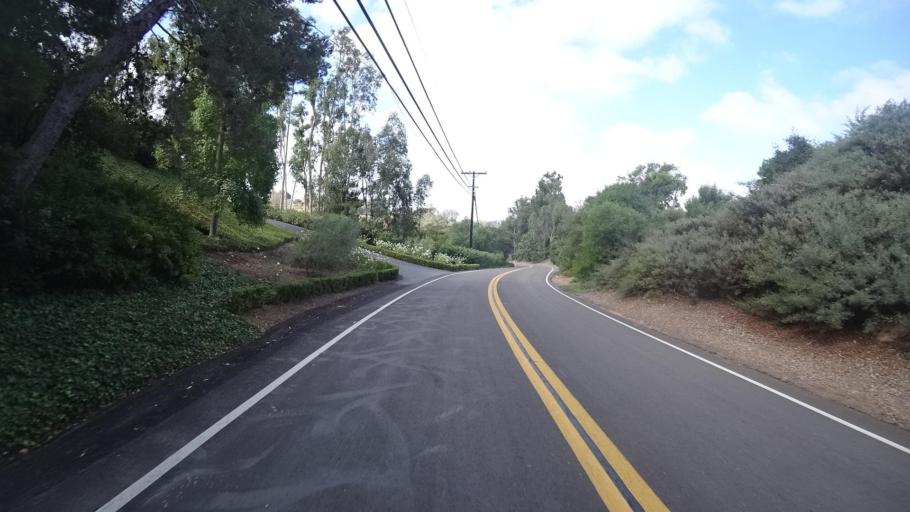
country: US
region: California
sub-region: San Diego County
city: Rancho Santa Fe
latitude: 33.0174
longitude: -117.2151
